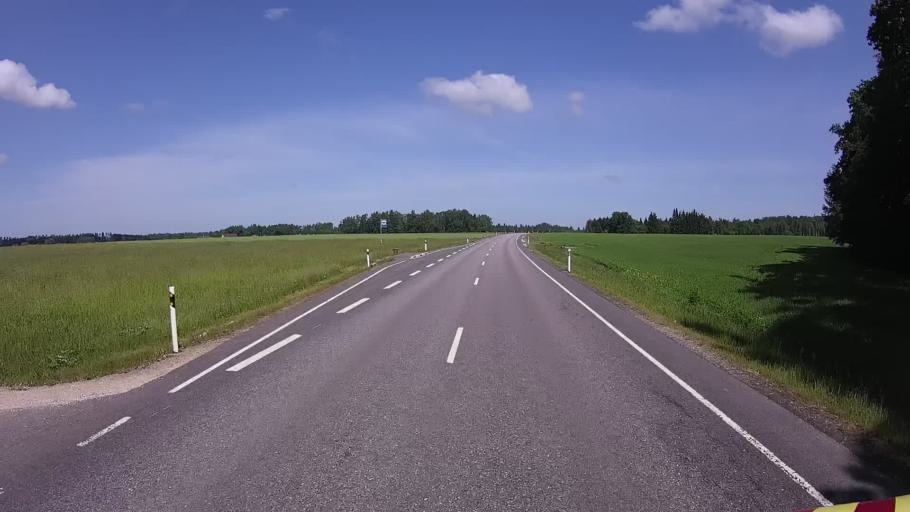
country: EE
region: Tartu
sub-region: Tartu linn
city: Tartu
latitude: 58.3726
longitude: 26.8839
